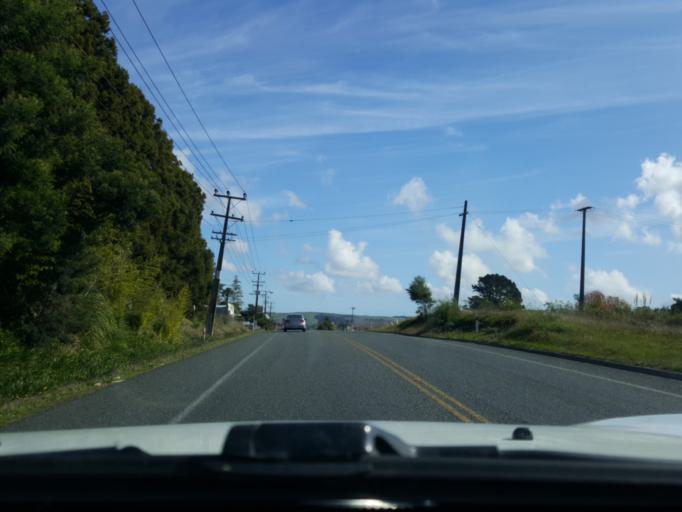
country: NZ
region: Auckland
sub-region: Auckland
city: Muriwai Beach
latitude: -36.7667
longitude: 174.5183
